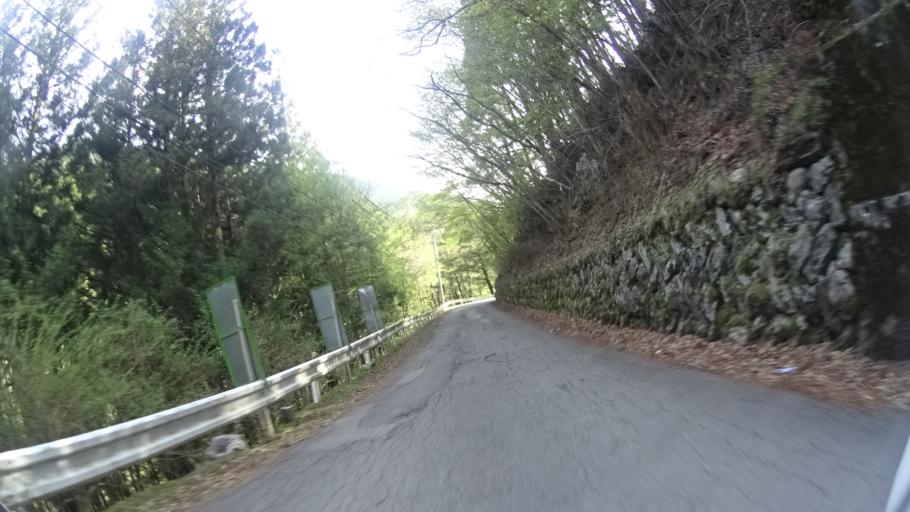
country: JP
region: Tokushima
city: Wakimachi
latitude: 33.8579
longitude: 134.0525
